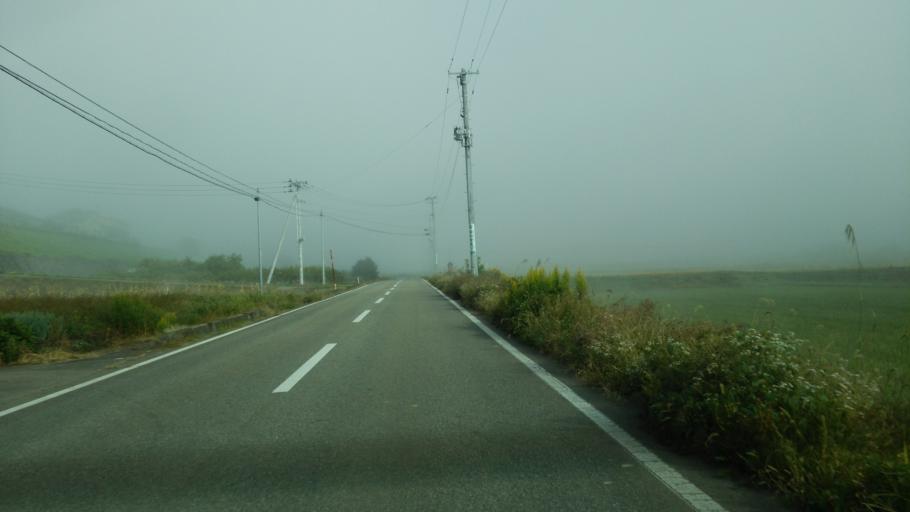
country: JP
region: Fukushima
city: Kitakata
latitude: 37.5092
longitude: 139.8233
